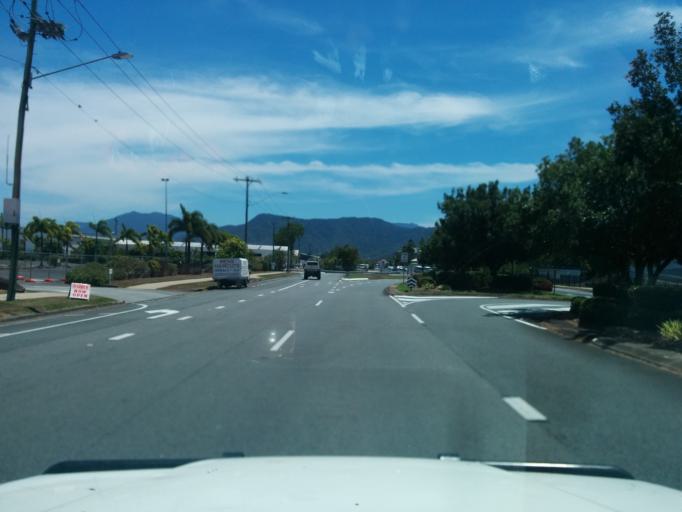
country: AU
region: Queensland
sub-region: Cairns
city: Cairns
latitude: -16.9310
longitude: 145.7682
